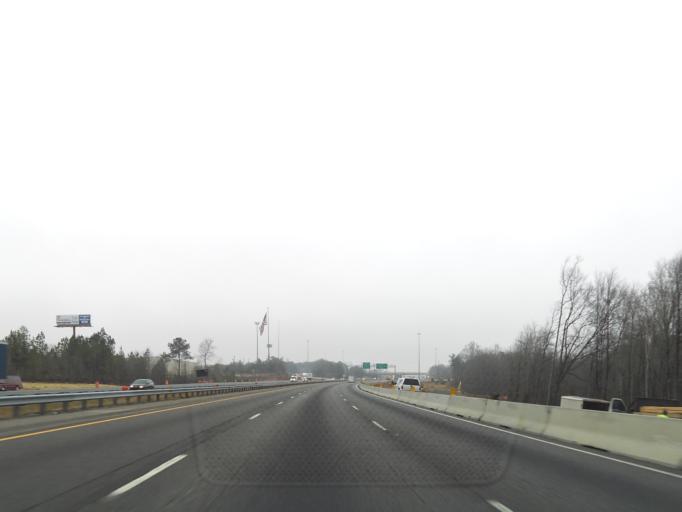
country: US
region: Georgia
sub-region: Henry County
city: McDonough
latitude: 33.4561
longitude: -84.2068
